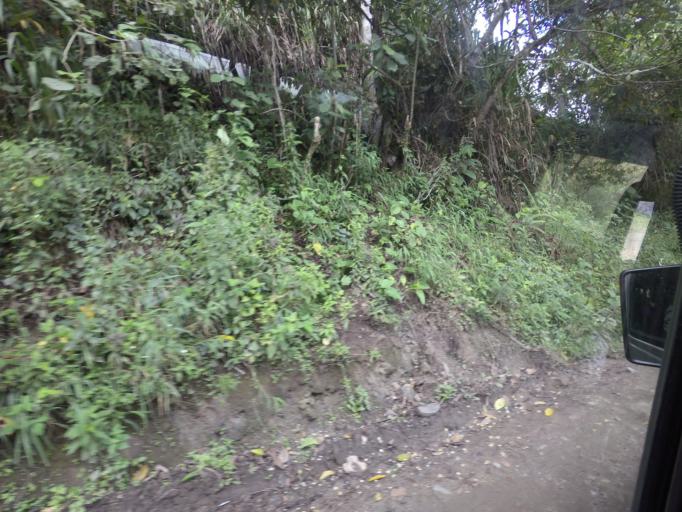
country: CO
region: Huila
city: San Agustin
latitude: 1.9220
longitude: -76.2987
